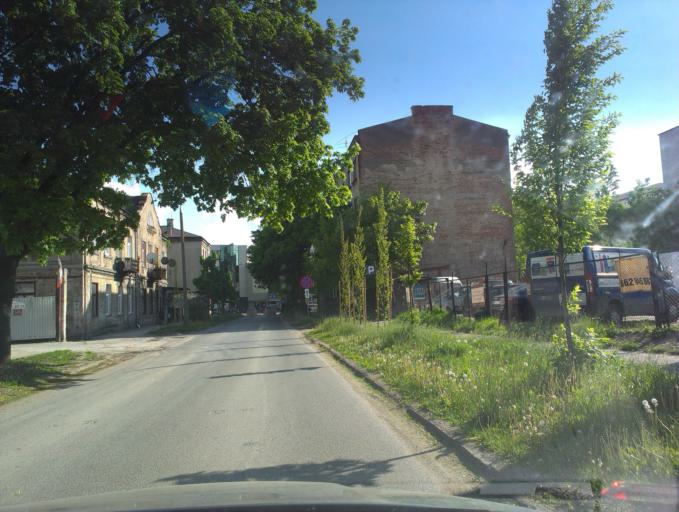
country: PL
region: Masovian Voivodeship
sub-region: Radom
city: Radom
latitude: 51.4009
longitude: 21.1654
